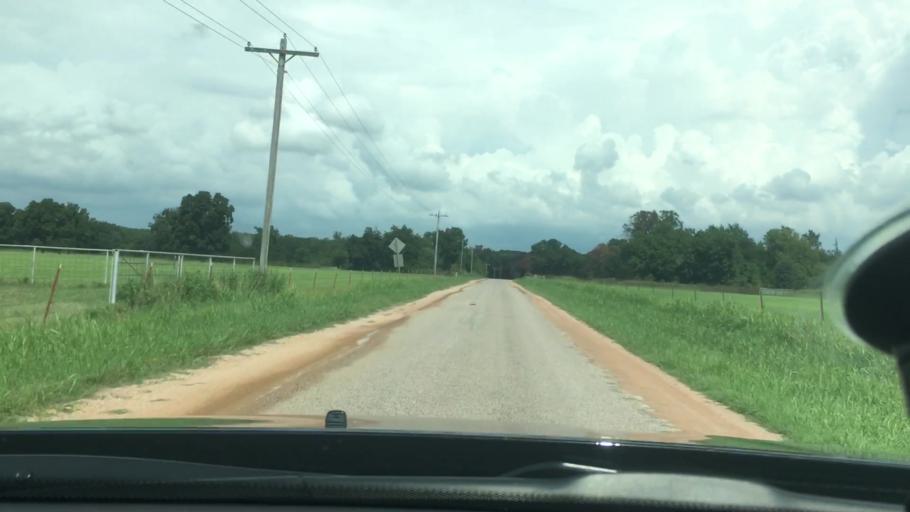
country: US
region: Oklahoma
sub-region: Carter County
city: Dickson
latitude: 34.2363
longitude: -96.9157
